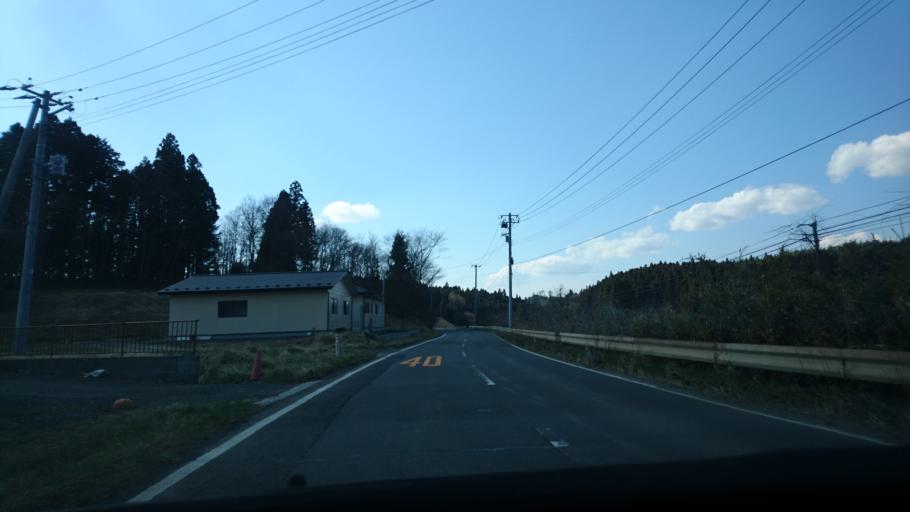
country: JP
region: Miyagi
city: Wakuya
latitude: 38.7101
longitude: 141.3211
